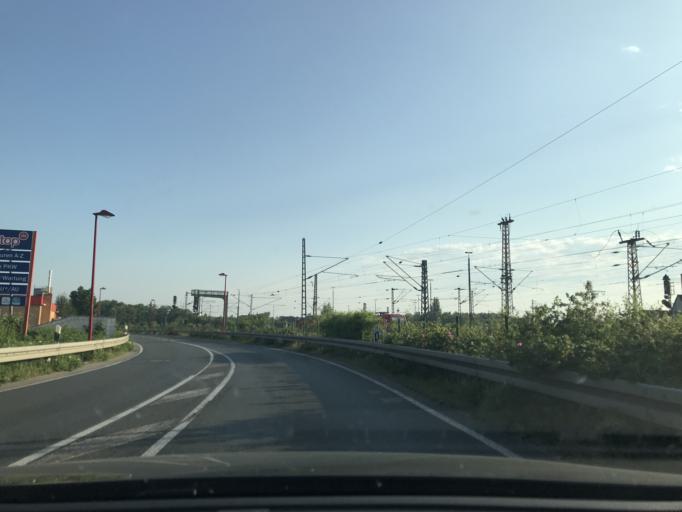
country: DE
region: Lower Saxony
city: Lehrte
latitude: 52.3837
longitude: 9.9732
